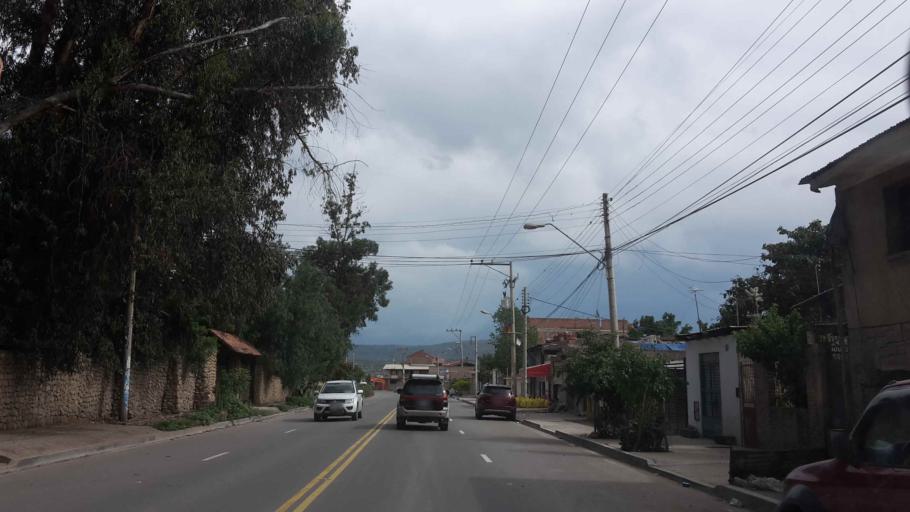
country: BO
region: Cochabamba
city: Cochabamba
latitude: -17.3806
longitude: -66.2515
